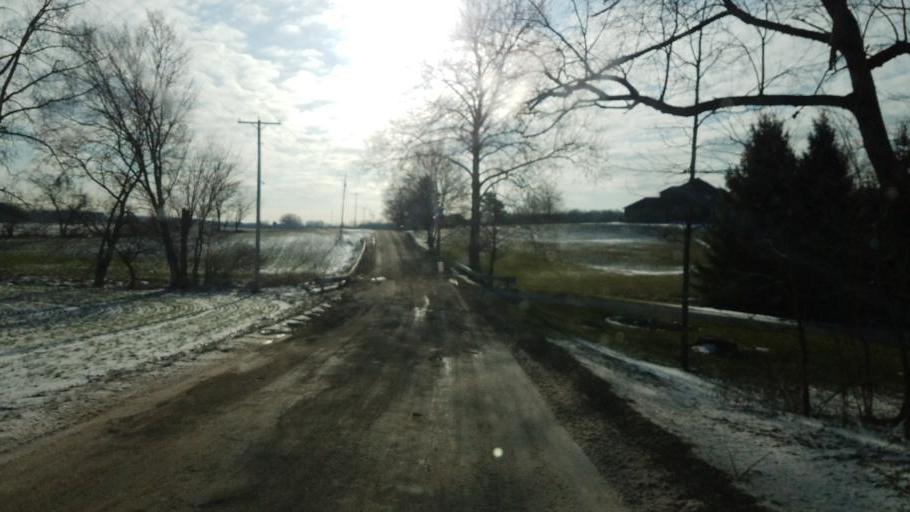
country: US
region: Ohio
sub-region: Richland County
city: Lexington
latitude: 40.6260
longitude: -82.6359
